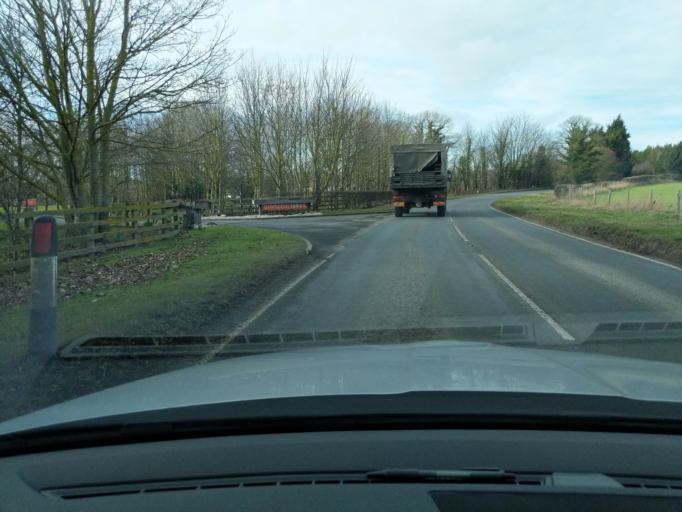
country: GB
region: England
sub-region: North Yorkshire
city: Catterick Garrison
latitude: 54.3956
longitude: -1.6869
